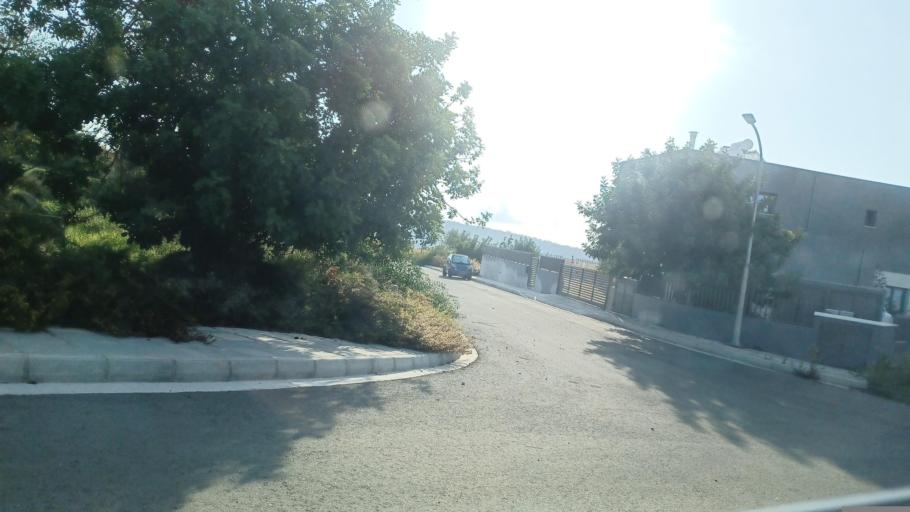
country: CY
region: Pafos
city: Mesogi
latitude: 34.7967
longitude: 32.4868
